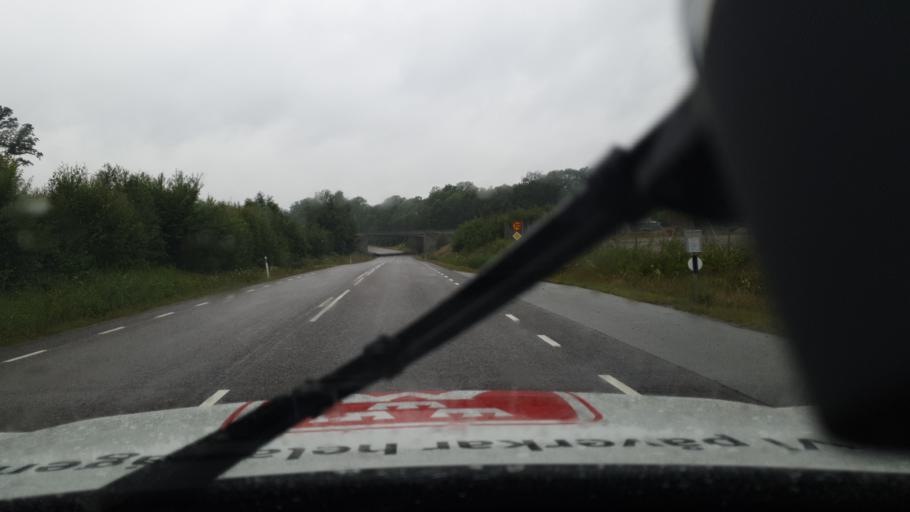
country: SE
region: Vaestra Goetaland
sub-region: Stenungsunds Kommun
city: Stora Hoga
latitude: 58.0606
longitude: 11.8886
